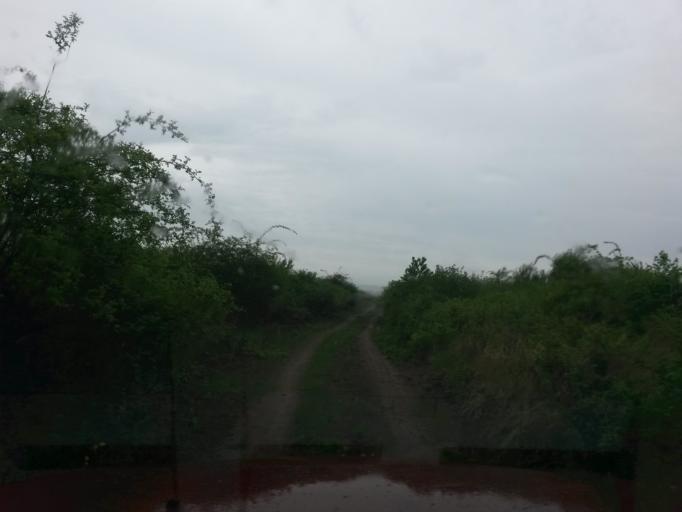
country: HU
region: Borsod-Abauj-Zemplen
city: Gonc
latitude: 48.5117
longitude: 21.3344
